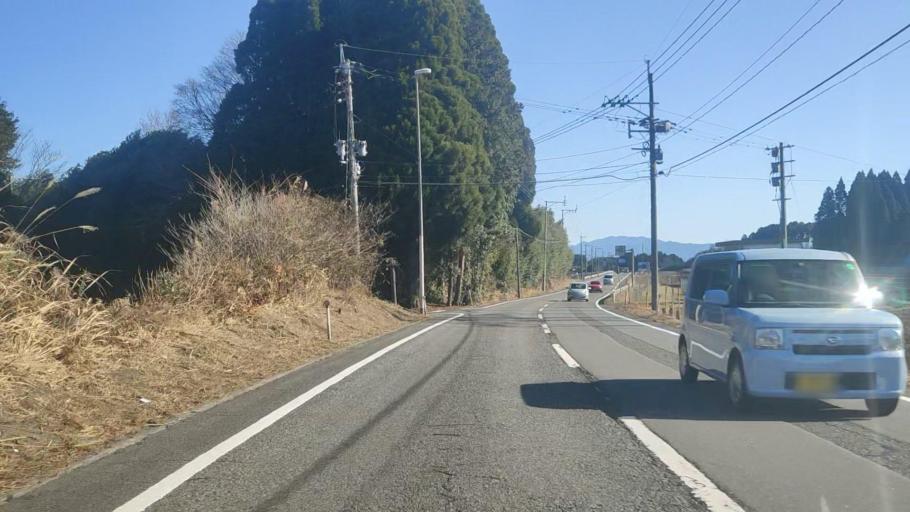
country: JP
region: Kagoshima
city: Sueyoshicho-ninokata
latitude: 31.6886
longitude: 130.9553
